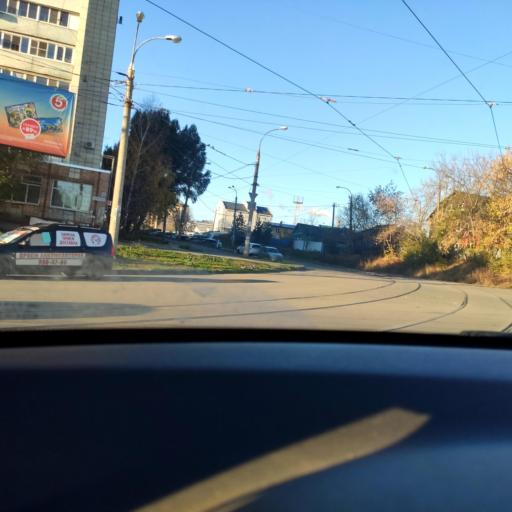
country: RU
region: Samara
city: Samara
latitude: 53.2170
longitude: 50.2221
